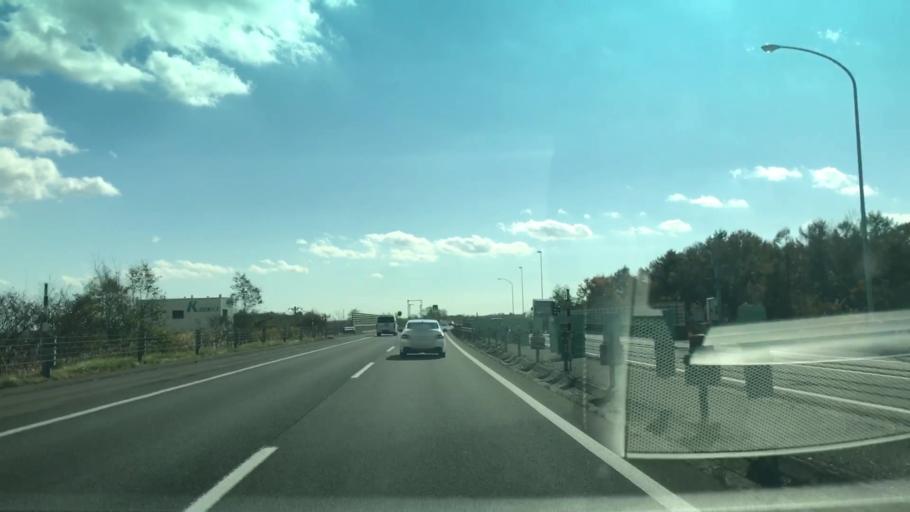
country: JP
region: Hokkaido
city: Kitahiroshima
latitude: 42.9099
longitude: 141.5501
